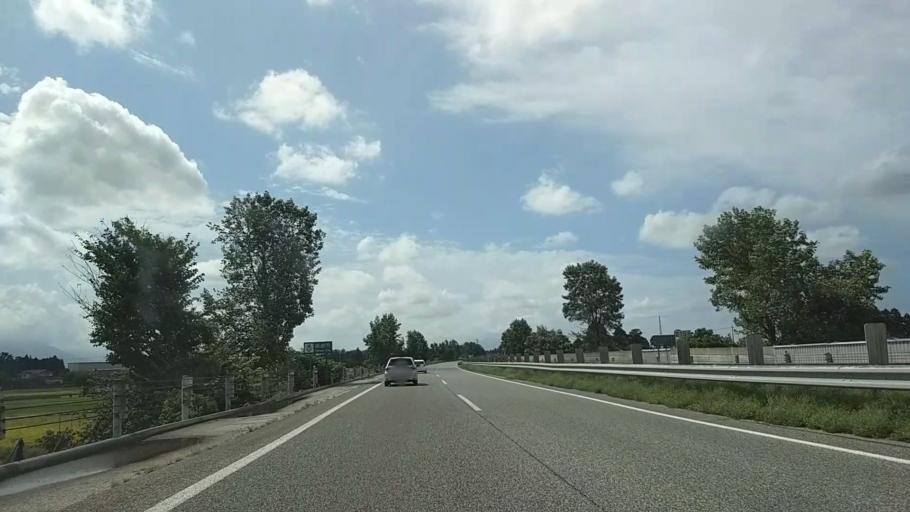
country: JP
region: Toyama
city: Takaoka
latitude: 36.6660
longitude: 137.0272
